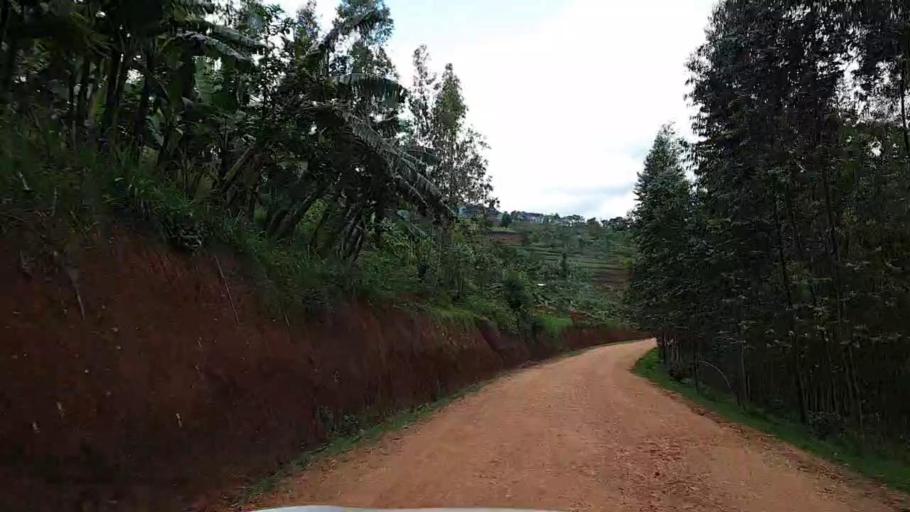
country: RW
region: Southern Province
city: Nyanza
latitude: -2.4087
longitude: 29.6759
